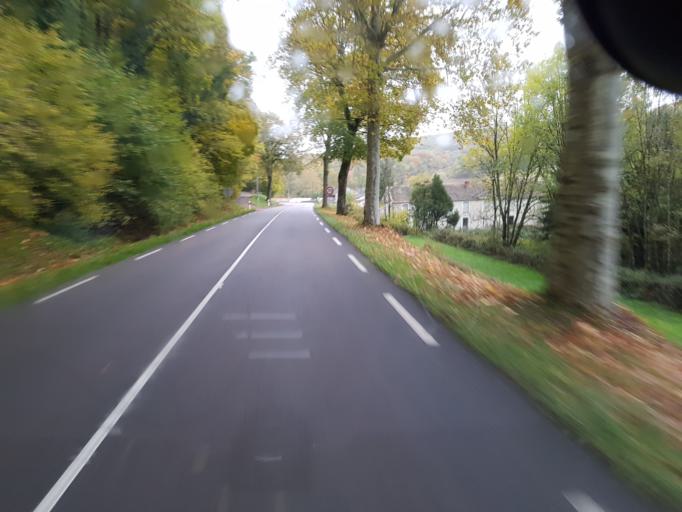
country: FR
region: Bourgogne
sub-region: Departement de la Cote-d'Or
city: Chatillon-sur-Seine
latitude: 47.7097
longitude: 4.5996
